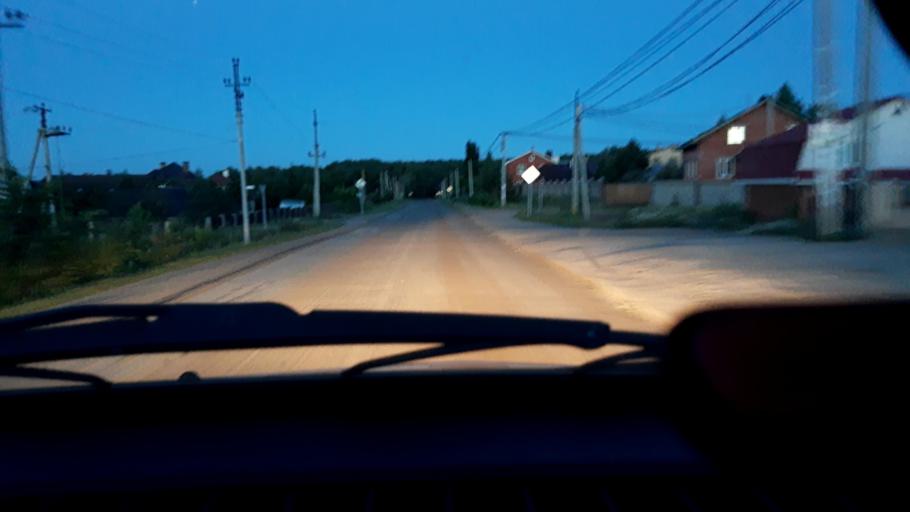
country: RU
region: Bashkortostan
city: Avdon
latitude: 54.6427
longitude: 55.7034
